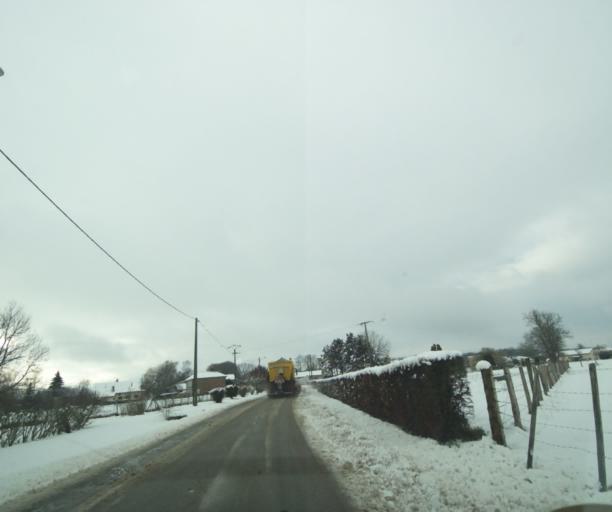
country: FR
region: Champagne-Ardenne
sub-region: Departement de la Haute-Marne
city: Montier-en-Der
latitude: 48.4920
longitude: 4.6998
